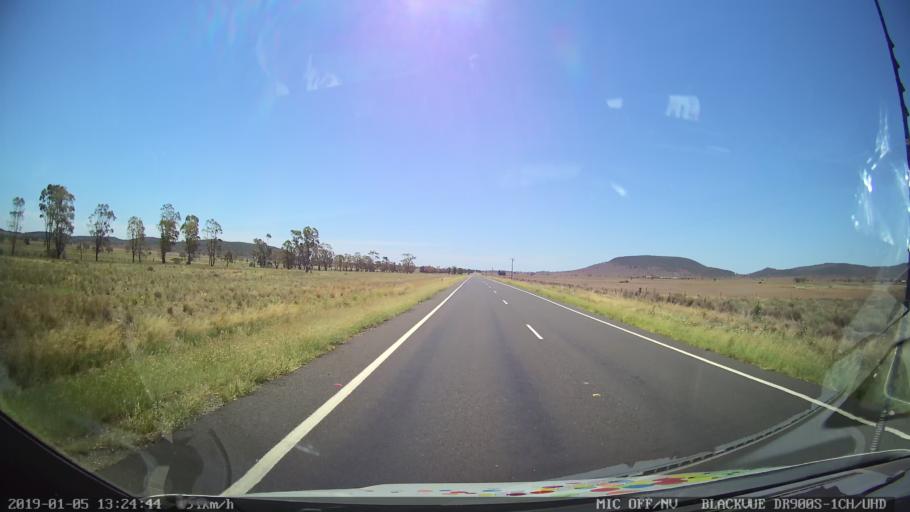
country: AU
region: New South Wales
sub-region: Gunnedah
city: Gunnedah
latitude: -31.0669
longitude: 149.9930
